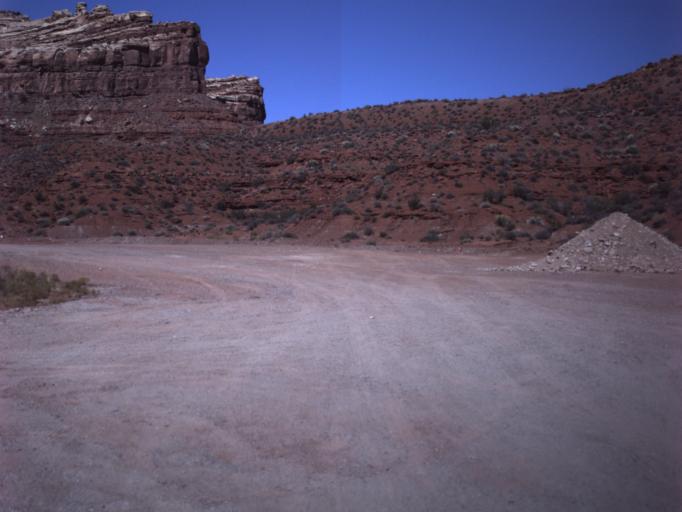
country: US
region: Utah
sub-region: San Juan County
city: Blanding
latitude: 37.2671
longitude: -109.9347
